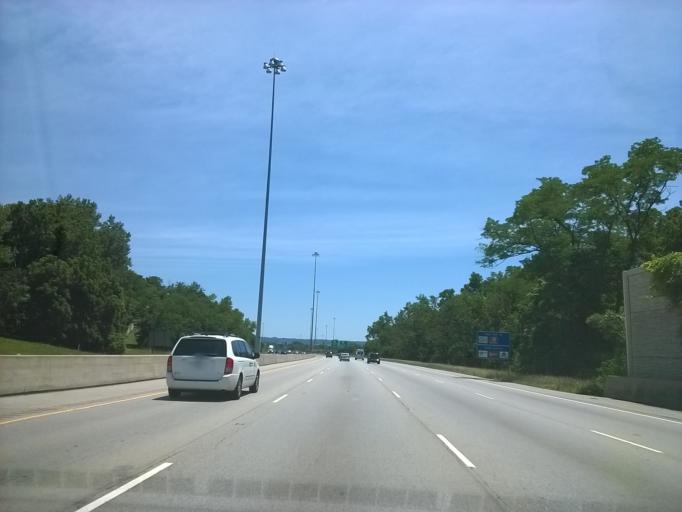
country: US
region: Ohio
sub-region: Hamilton County
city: Forest Park
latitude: 39.2959
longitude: -84.4953
